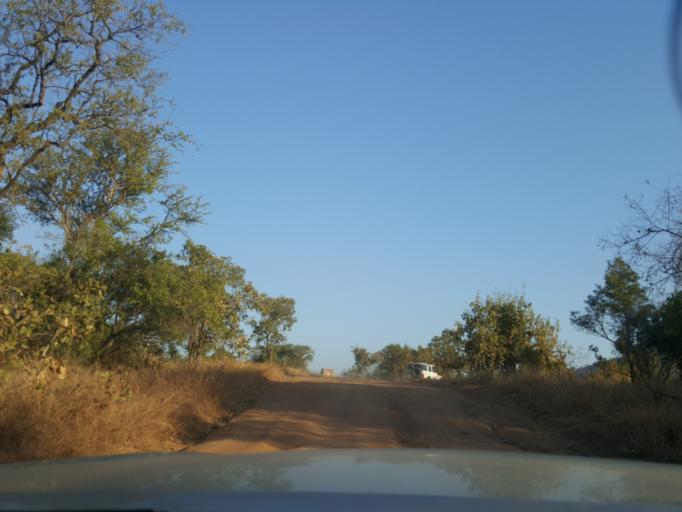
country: SZ
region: Hhohho
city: Ntfonjeni
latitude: -25.4232
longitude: 31.4425
